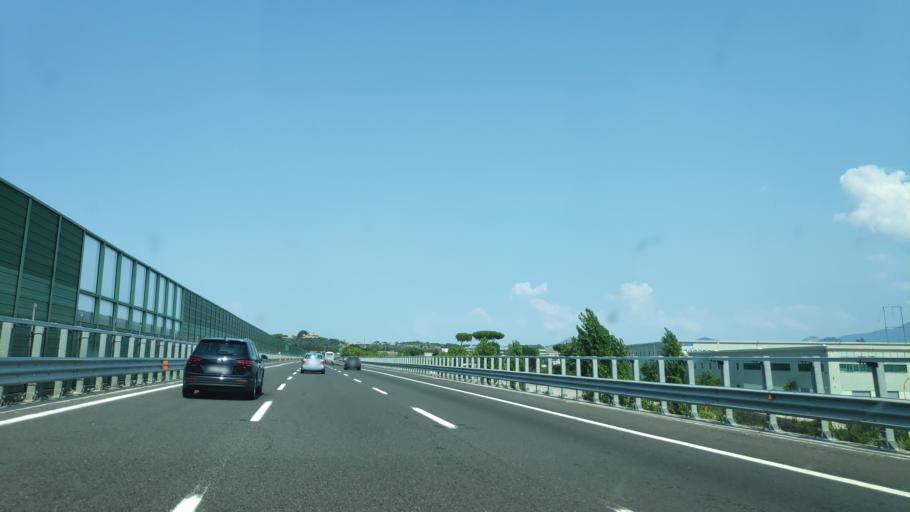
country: IT
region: Latium
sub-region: Citta metropolitana di Roma Capitale
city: Albuccione
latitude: 41.9540
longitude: 12.7017
